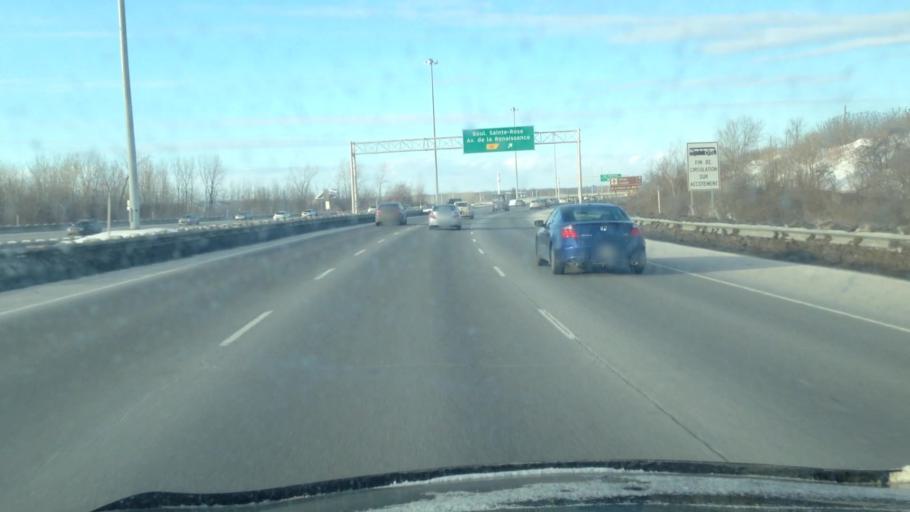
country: CA
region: Quebec
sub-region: Laurentides
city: Boisbriand
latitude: 45.5936
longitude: -73.8022
